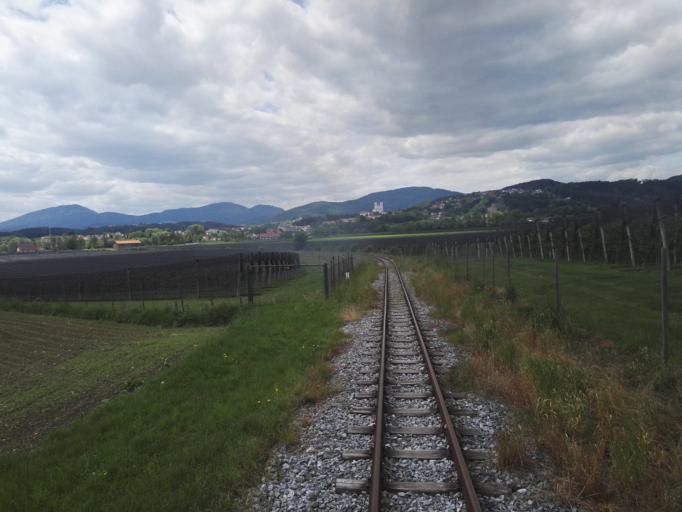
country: AT
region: Styria
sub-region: Politischer Bezirk Weiz
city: Krottendorf
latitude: 47.2179
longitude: 15.6565
